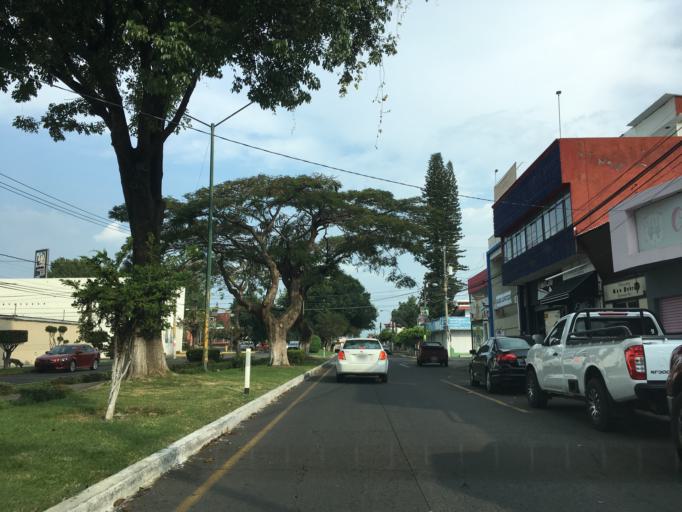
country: MX
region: Michoacan
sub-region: Uruapan
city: Uruapan
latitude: 19.4069
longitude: -102.0557
